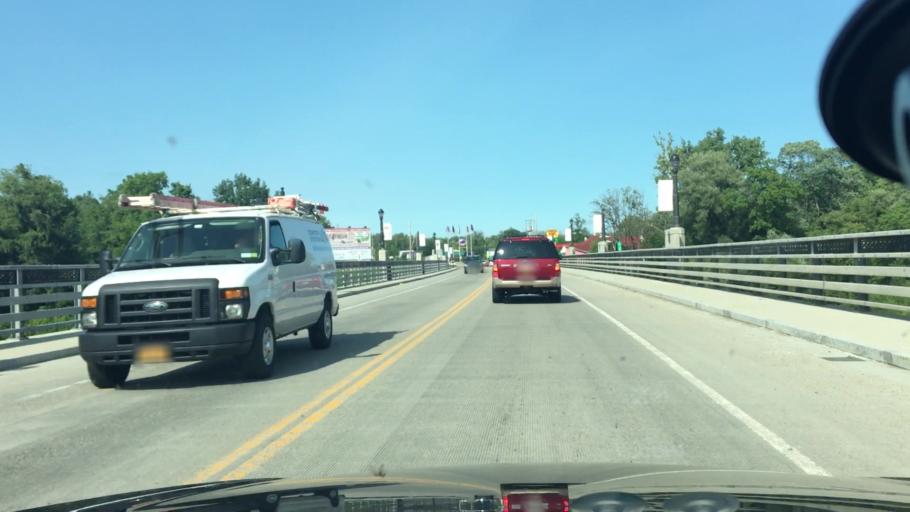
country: US
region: New York
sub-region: Chautauqua County
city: Silver Creek
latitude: 42.5677
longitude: -79.1048
